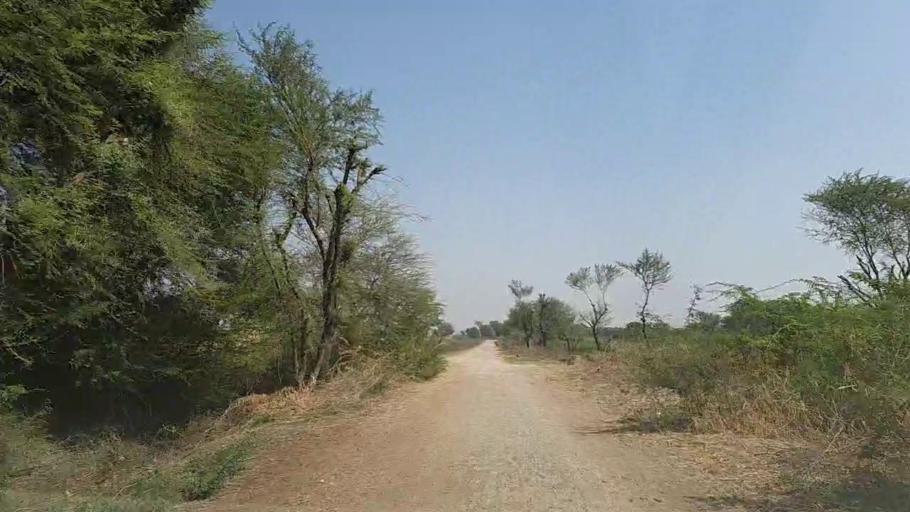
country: PK
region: Sindh
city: Samaro
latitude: 25.2432
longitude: 69.4121
